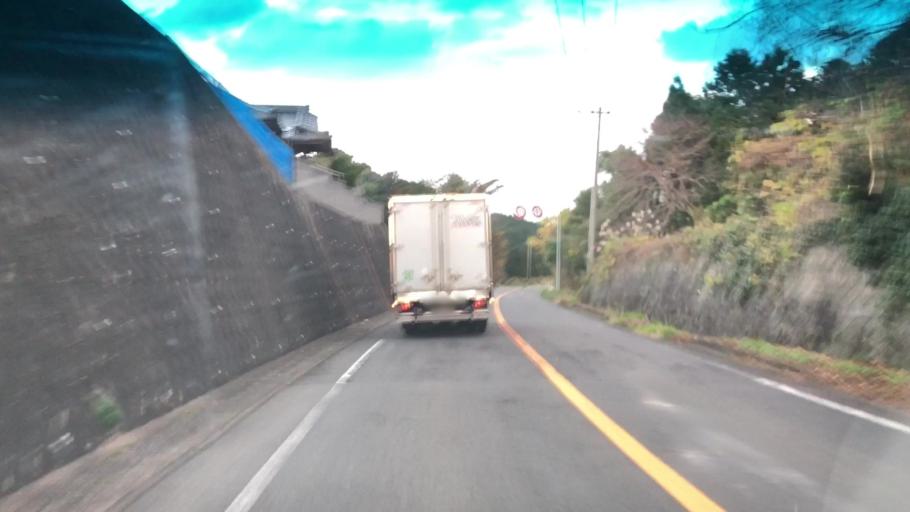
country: JP
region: Nagasaki
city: Sasebo
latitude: 33.0472
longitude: 129.7126
